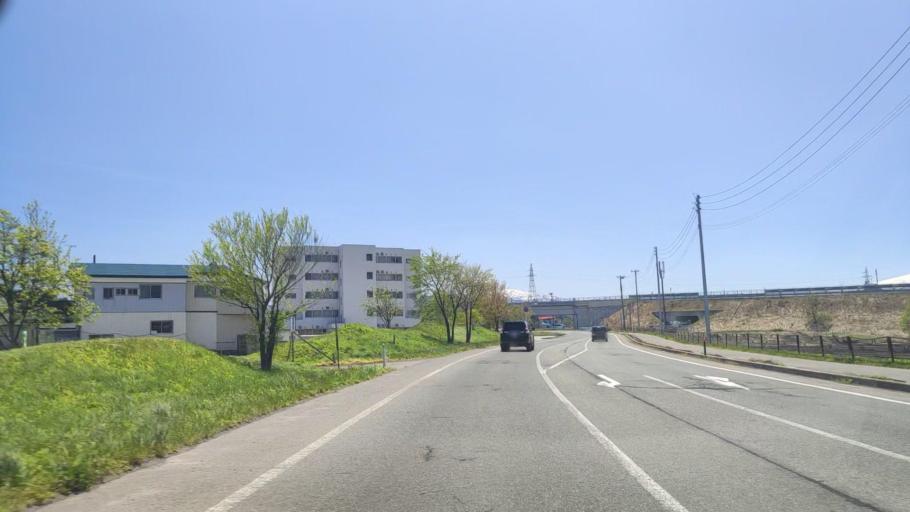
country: JP
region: Yamagata
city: Shinjo
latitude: 38.7467
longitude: 140.2955
